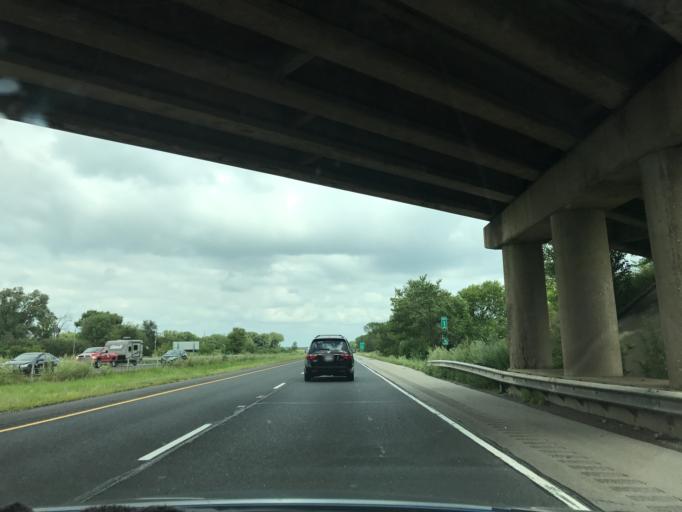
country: US
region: Illinois
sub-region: Grundy County
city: Minooka
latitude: 41.4702
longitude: -88.2411
